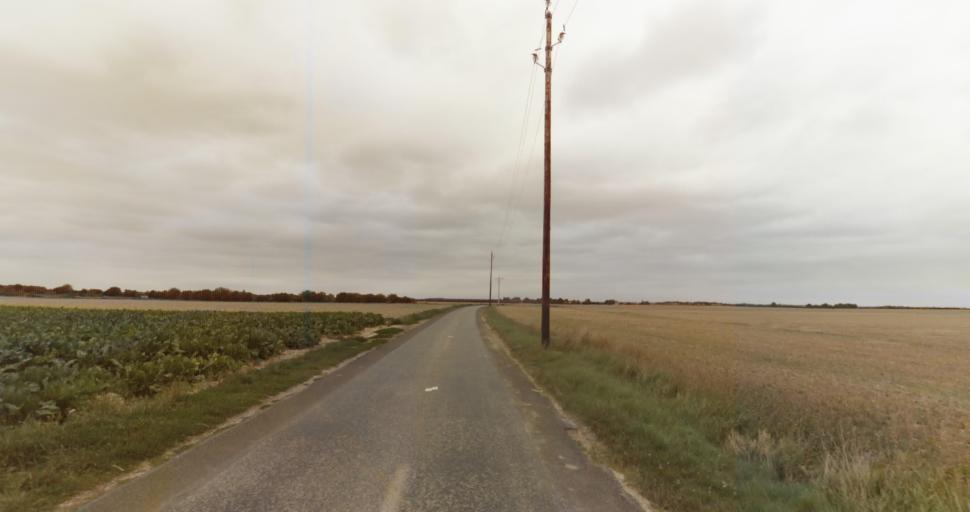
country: FR
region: Haute-Normandie
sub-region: Departement de l'Eure
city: La Couture-Boussey
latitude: 48.9223
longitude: 1.3068
